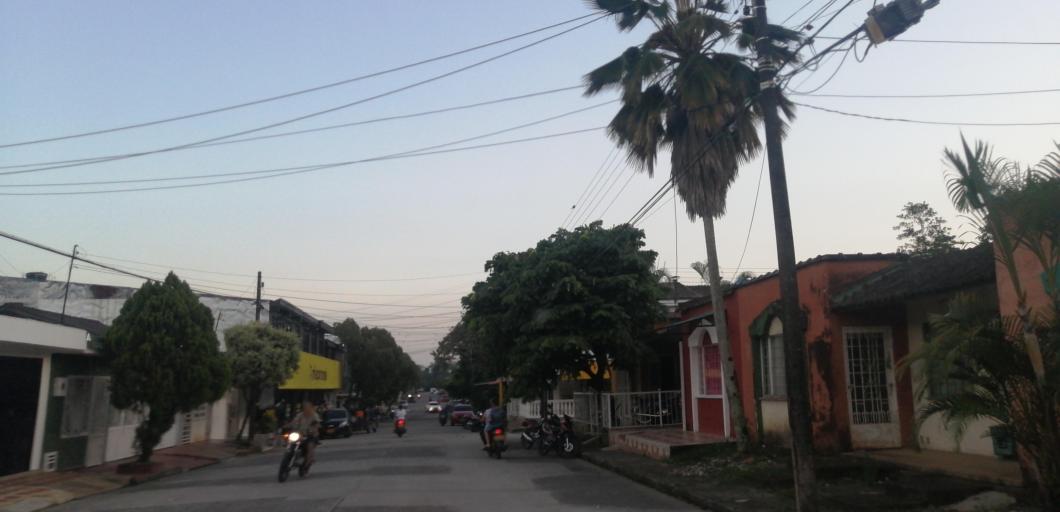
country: CO
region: Meta
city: Acacias
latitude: 3.9933
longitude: -73.7581
